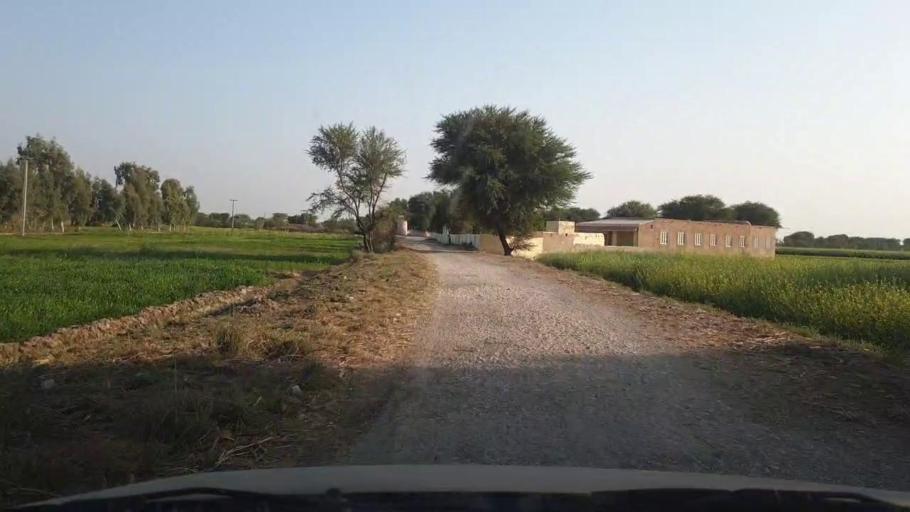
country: PK
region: Sindh
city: Samaro
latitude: 25.2747
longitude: 69.3628
